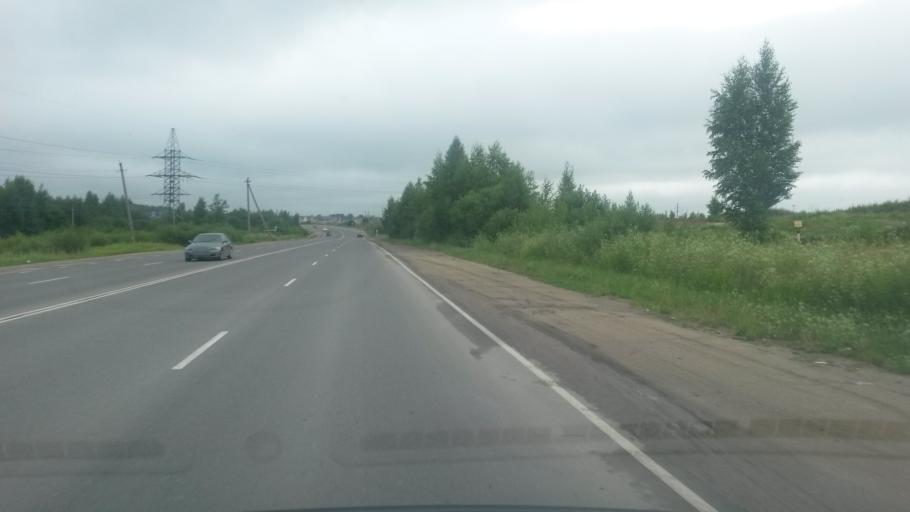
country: RU
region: Ivanovo
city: Novo-Talitsy
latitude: 57.0120
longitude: 40.8806
